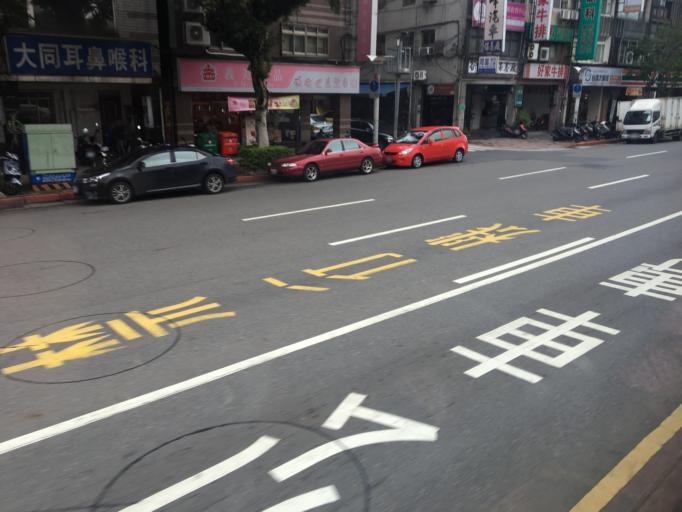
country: TW
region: Taipei
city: Taipei
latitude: 25.0711
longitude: 121.5138
